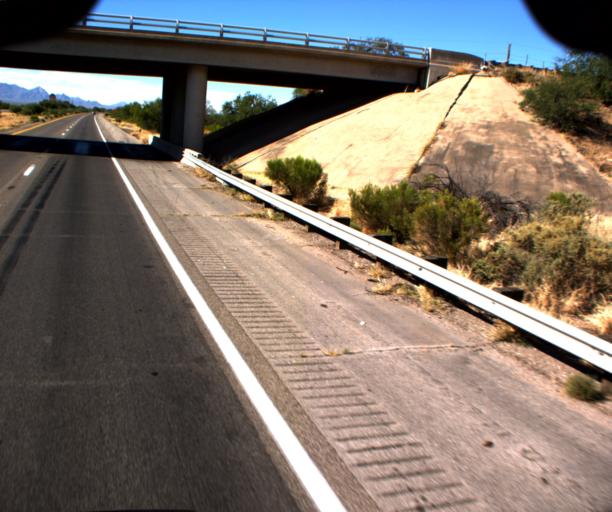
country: US
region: Arizona
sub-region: Pima County
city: Sahuarita
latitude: 31.9583
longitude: -110.9879
